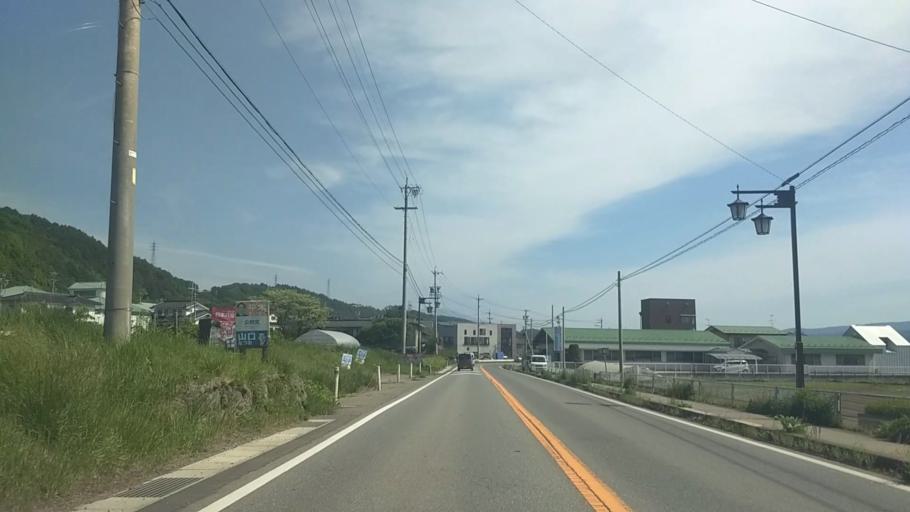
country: JP
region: Nagano
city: Saku
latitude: 36.1413
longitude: 138.4718
